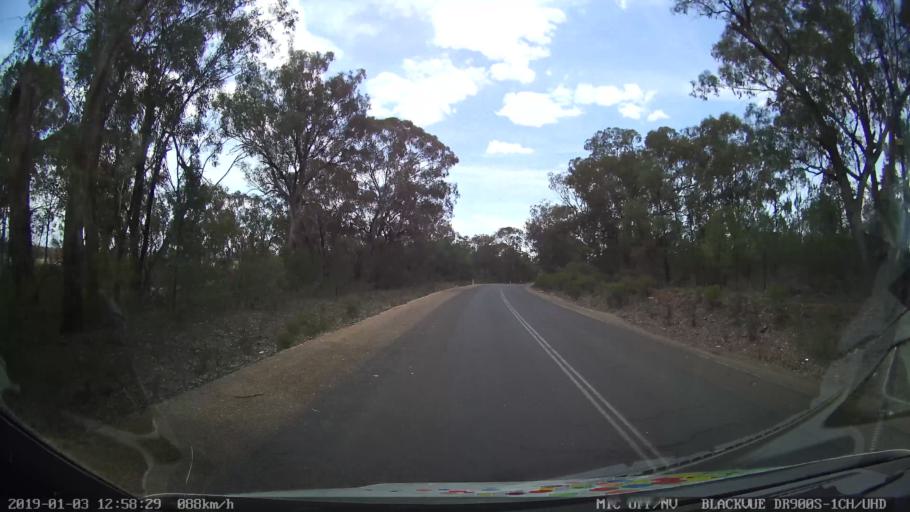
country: AU
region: New South Wales
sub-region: Cabonne
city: Canowindra
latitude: -33.6416
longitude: 148.3757
